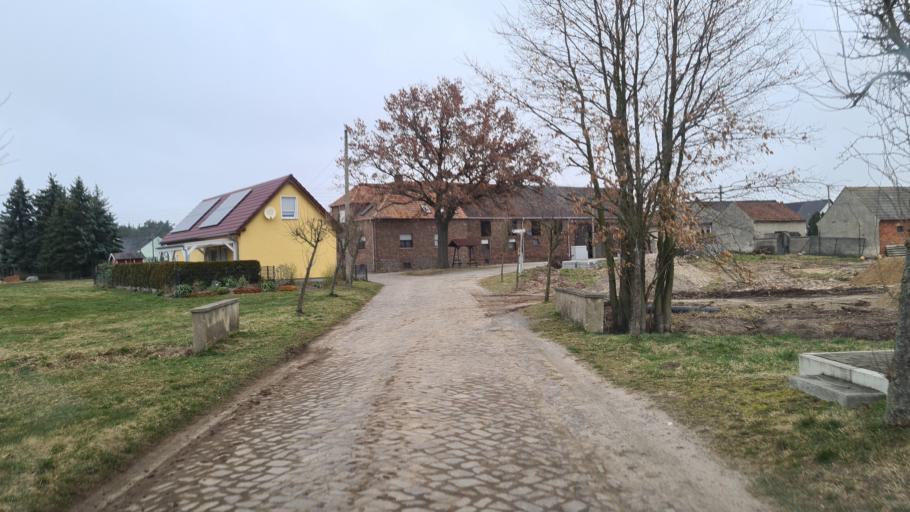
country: DE
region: Brandenburg
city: Herzberg
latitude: 51.6830
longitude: 13.1865
